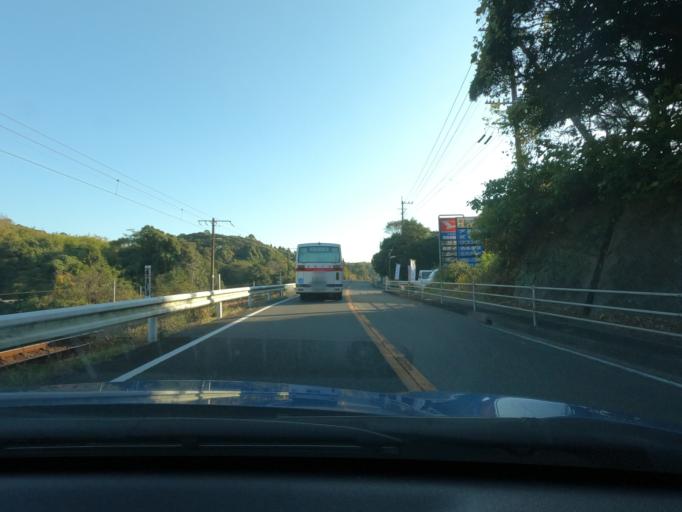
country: JP
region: Kagoshima
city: Akune
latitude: 31.9947
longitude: 130.1976
